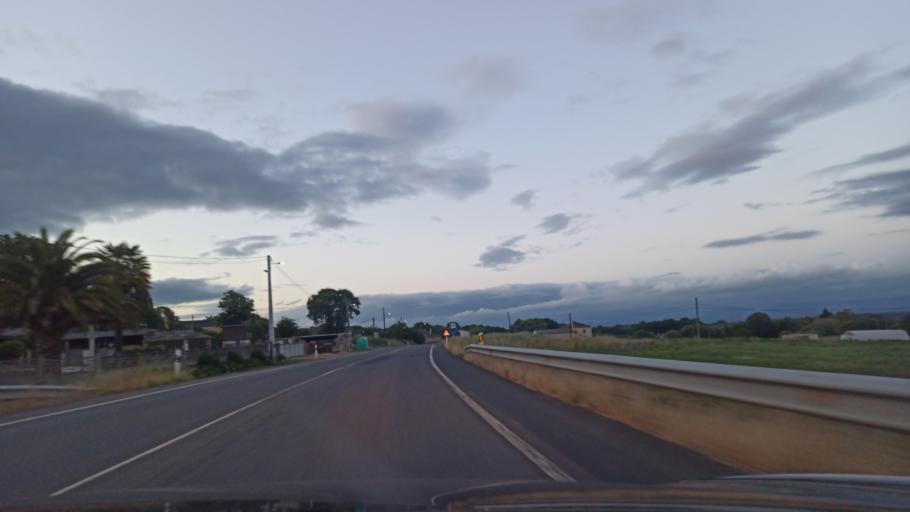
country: ES
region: Galicia
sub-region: Provincia de Lugo
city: Ourol
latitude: 42.9444
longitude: -7.6268
